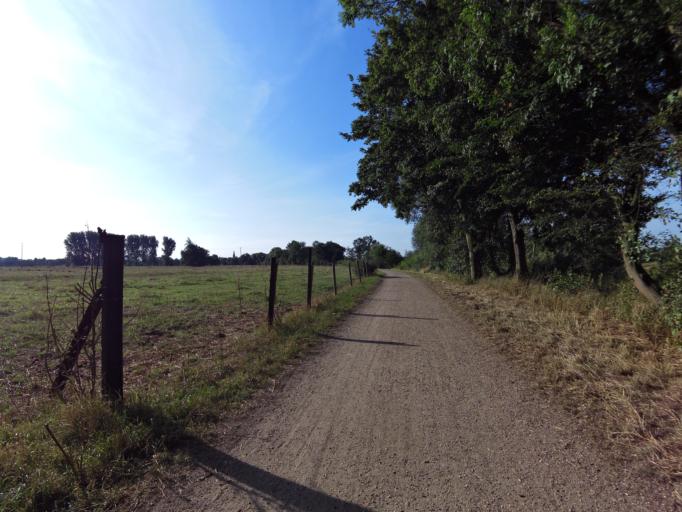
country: DE
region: North Rhine-Westphalia
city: Huckelhoven
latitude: 51.0454
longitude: 6.2092
